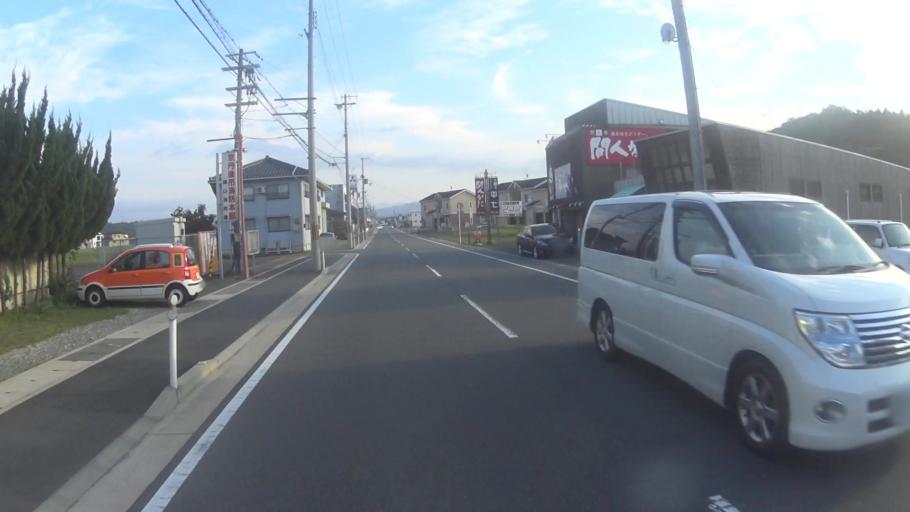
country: JP
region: Kyoto
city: Miyazu
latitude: 35.6255
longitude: 135.0728
